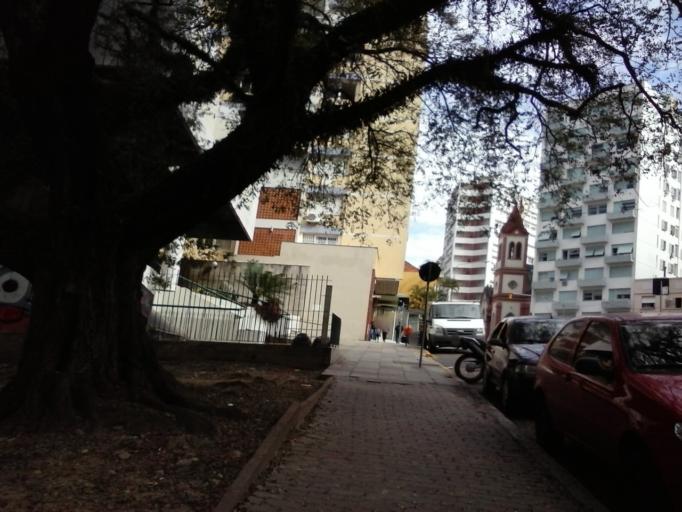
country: BR
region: Rio Grande do Sul
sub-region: Porto Alegre
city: Porto Alegre
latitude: -30.0320
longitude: -51.2242
